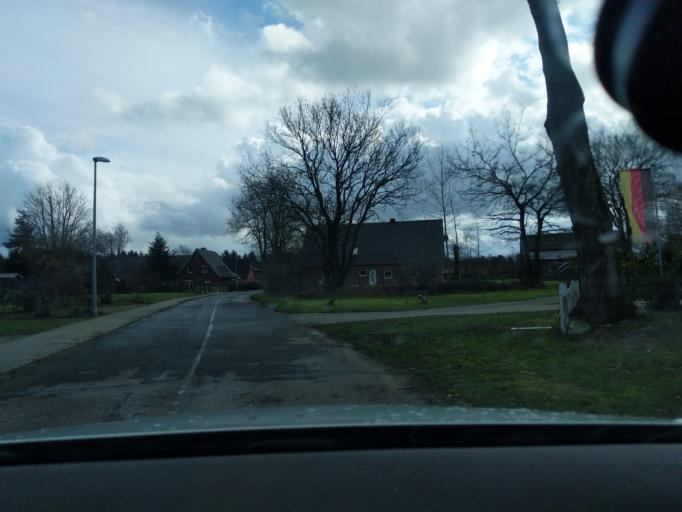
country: DE
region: Lower Saxony
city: Kranenburg
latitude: 53.6083
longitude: 9.2022
